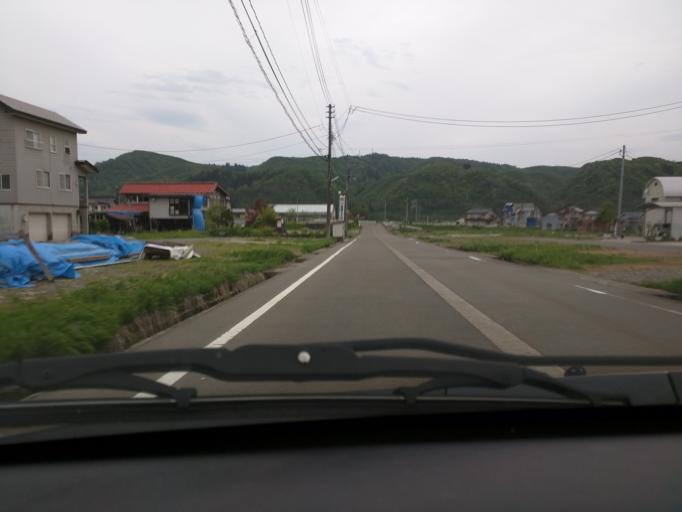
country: JP
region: Niigata
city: Muikamachi
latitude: 37.1937
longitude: 138.9522
